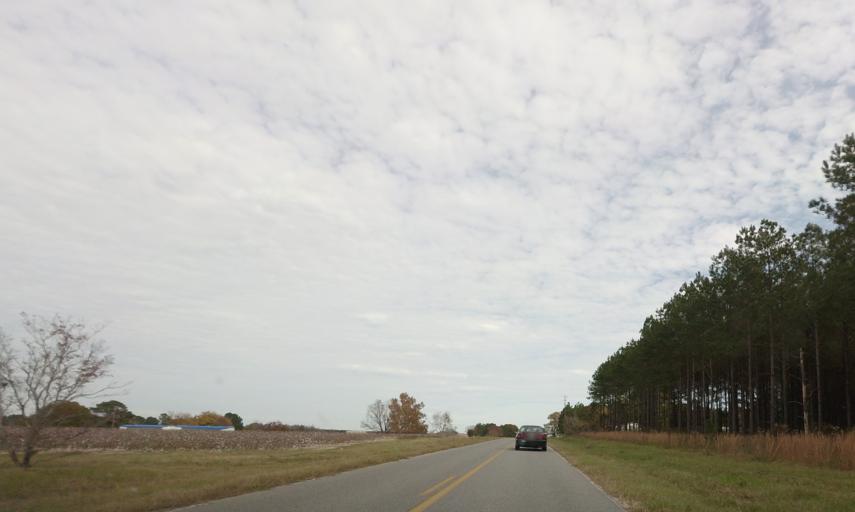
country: US
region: Georgia
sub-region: Dodge County
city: Chester
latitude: 32.4180
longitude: -83.1906
